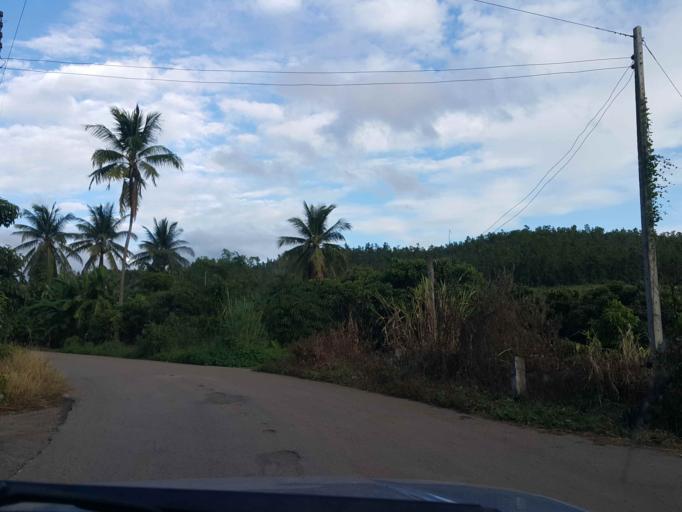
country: TH
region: Chiang Mai
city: Mae Chaem
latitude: 18.5155
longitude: 98.3985
